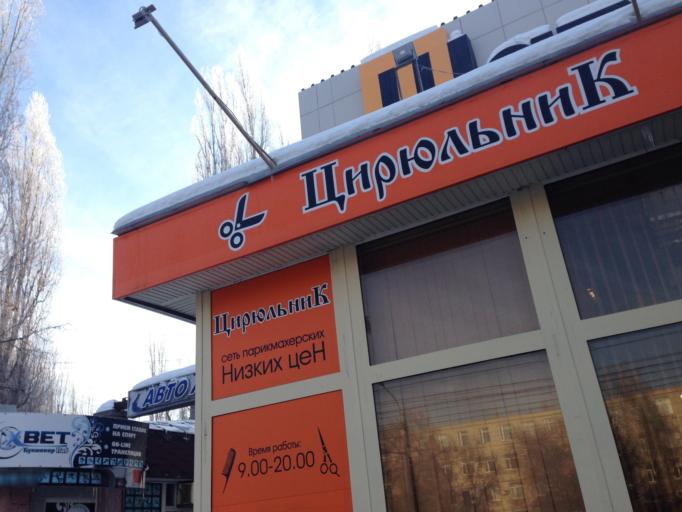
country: RU
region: Voronezj
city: Voronezh
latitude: 51.6601
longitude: 39.1512
